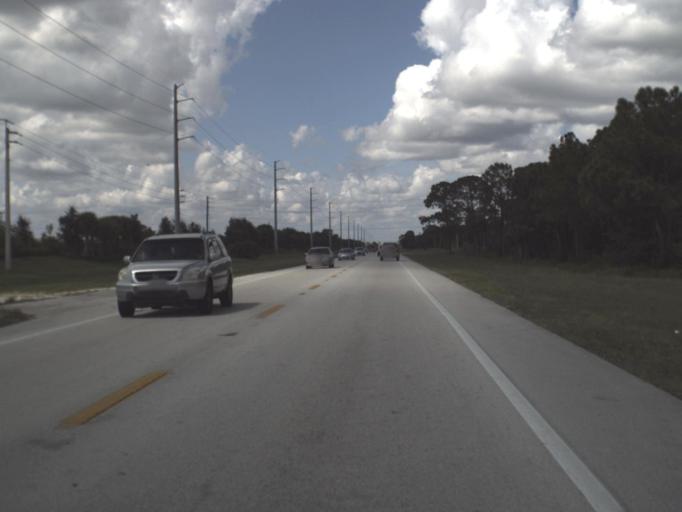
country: US
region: Florida
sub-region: Lee County
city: Gateway
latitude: 26.5977
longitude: -81.7437
